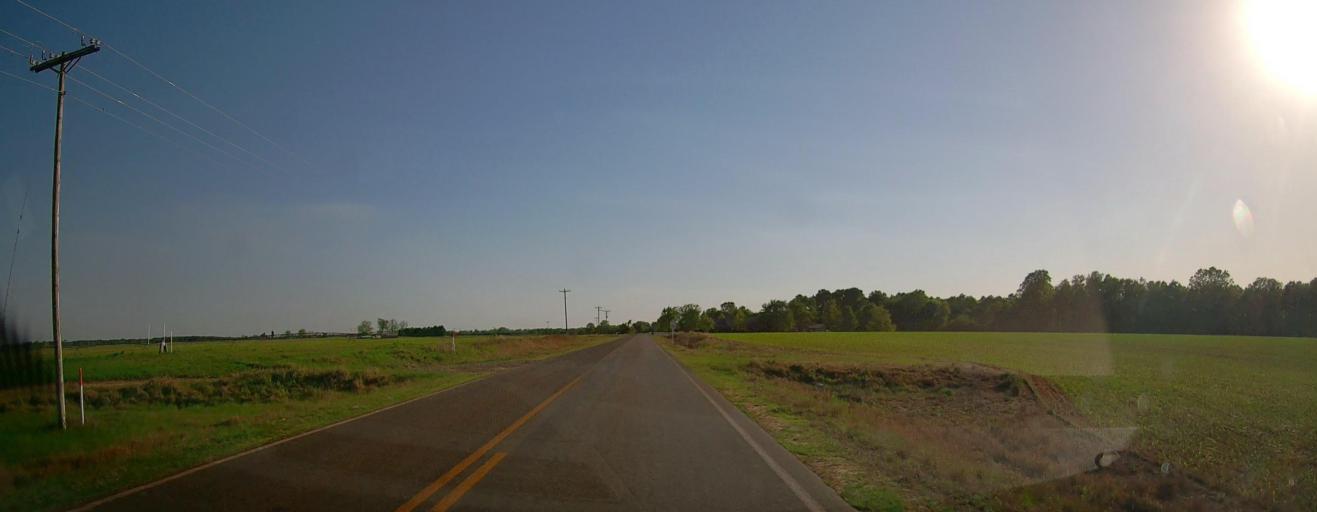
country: US
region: Georgia
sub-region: Macon County
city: Marshallville
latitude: 32.3560
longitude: -83.9410
